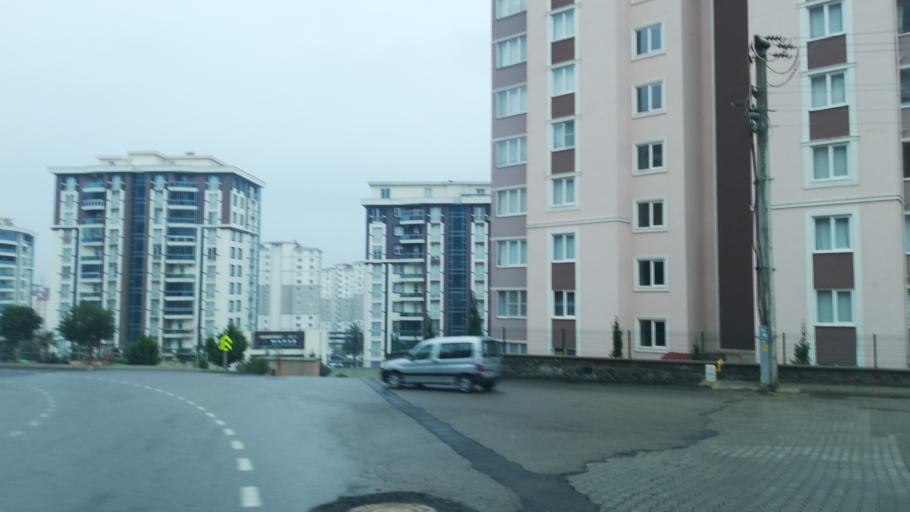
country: TR
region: Kahramanmaras
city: Kahramanmaras
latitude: 37.5947
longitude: 36.8513
